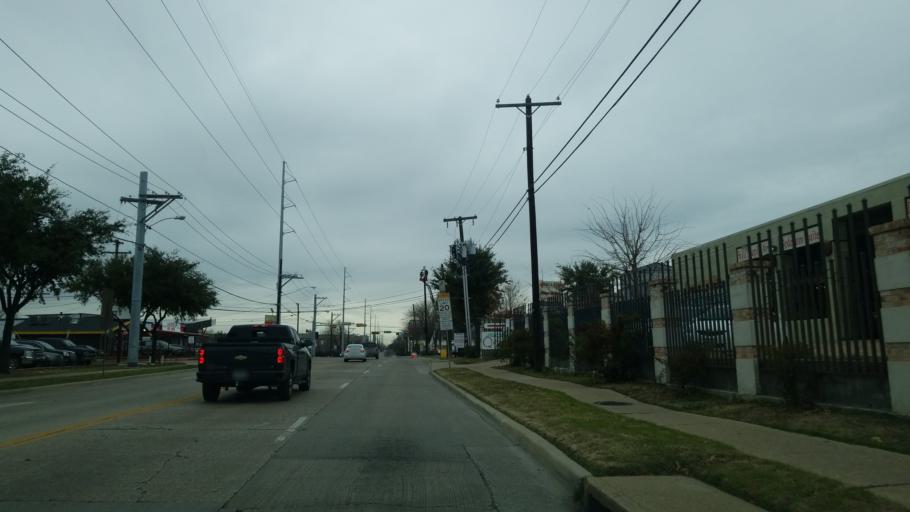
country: US
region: Texas
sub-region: Dallas County
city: Highland Park
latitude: 32.8204
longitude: -96.8352
